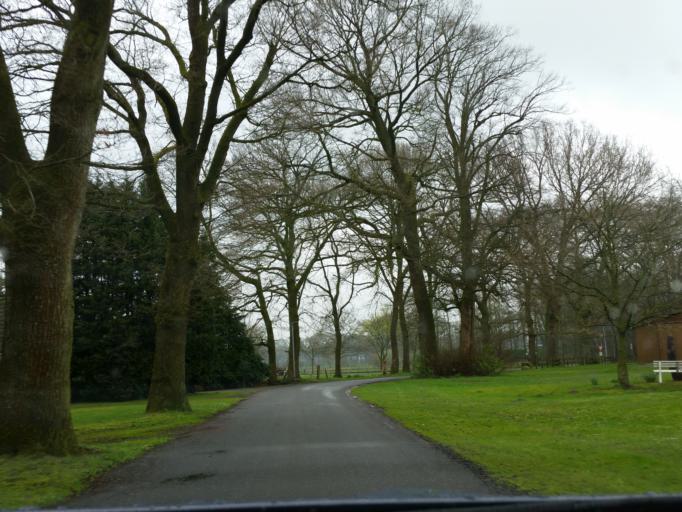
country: DE
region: Lower Saxony
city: Hipstedt
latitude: 53.4790
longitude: 8.9696
